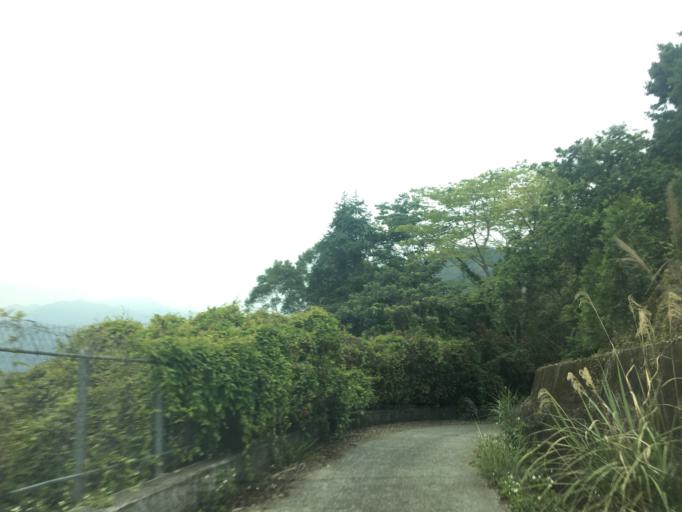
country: TW
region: Taiwan
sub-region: Taichung City
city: Taichung
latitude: 24.1467
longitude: 120.8216
